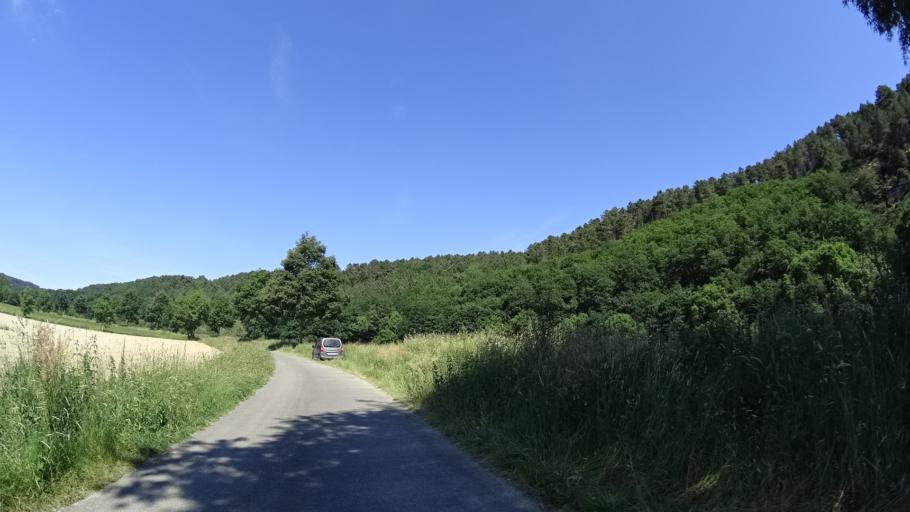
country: FR
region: Brittany
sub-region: Departement d'Ille-et-Vilaine
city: Langon
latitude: 47.7665
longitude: -1.8237
